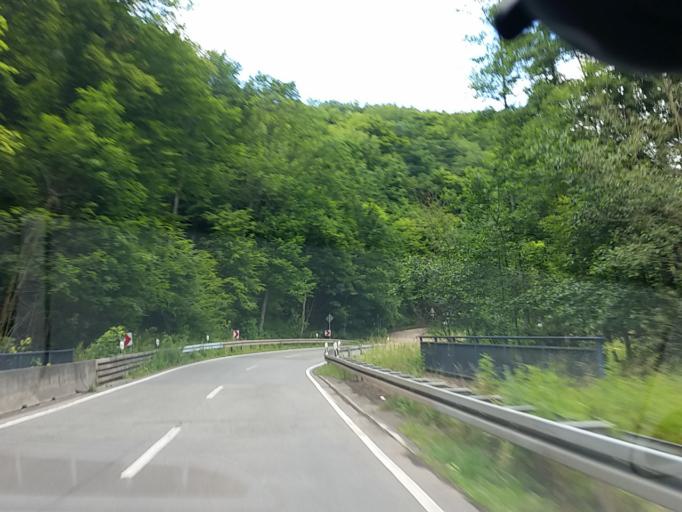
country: DE
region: Saarland
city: Schmelz
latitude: 49.4725
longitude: 6.8598
